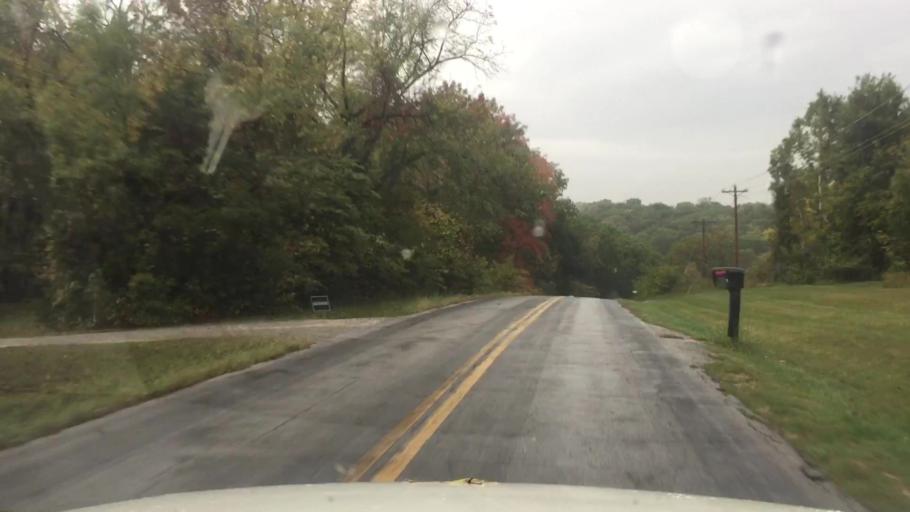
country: US
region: Missouri
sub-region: Boone County
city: Columbia
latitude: 38.9357
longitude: -92.4816
